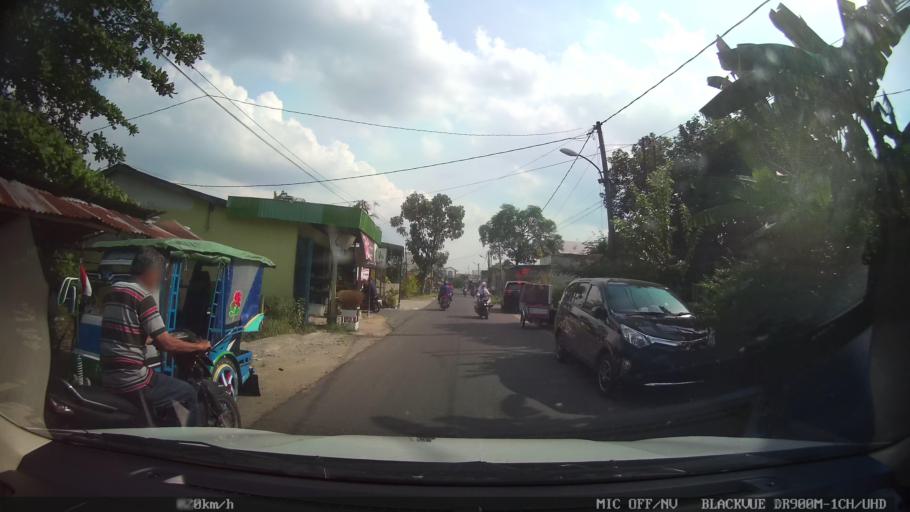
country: ID
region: North Sumatra
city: Binjai
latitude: 3.6122
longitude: 98.4985
